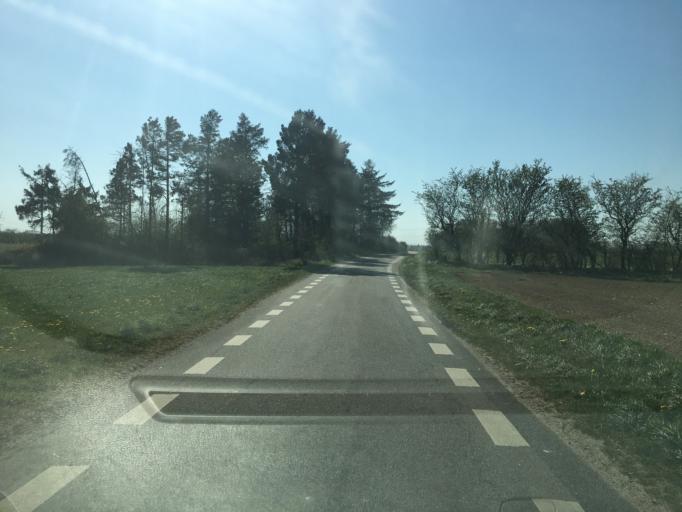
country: DK
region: South Denmark
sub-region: Aabenraa Kommune
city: Rodekro
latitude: 55.0674
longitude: 9.2774
